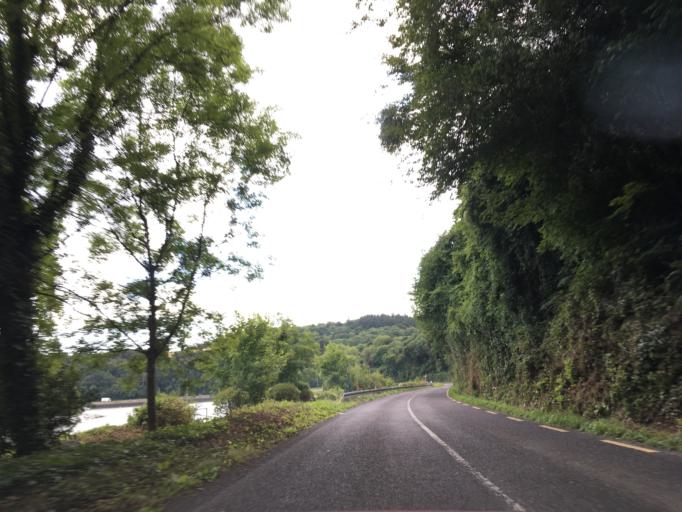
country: IE
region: Munster
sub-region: County Cork
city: Crosshaven
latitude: 51.8033
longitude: -8.3330
